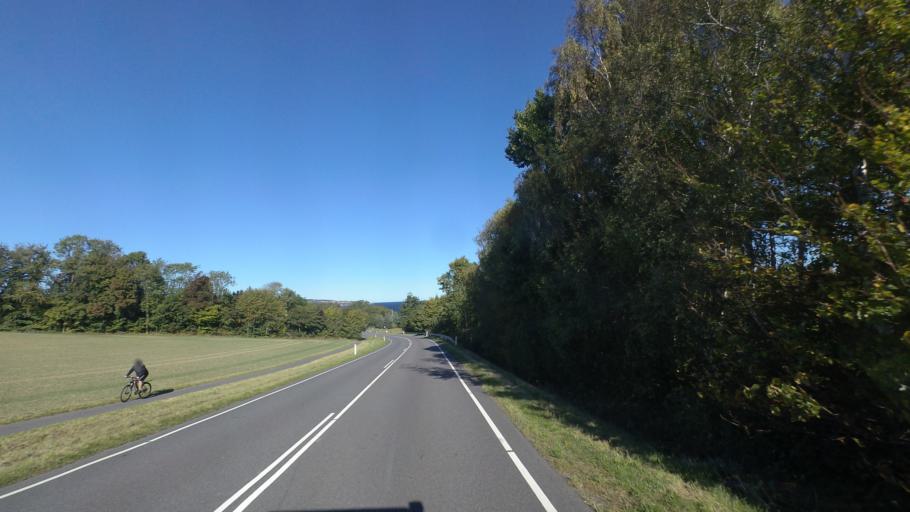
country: DK
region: Capital Region
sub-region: Bornholm Kommune
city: Akirkeby
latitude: 55.1738
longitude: 15.0243
